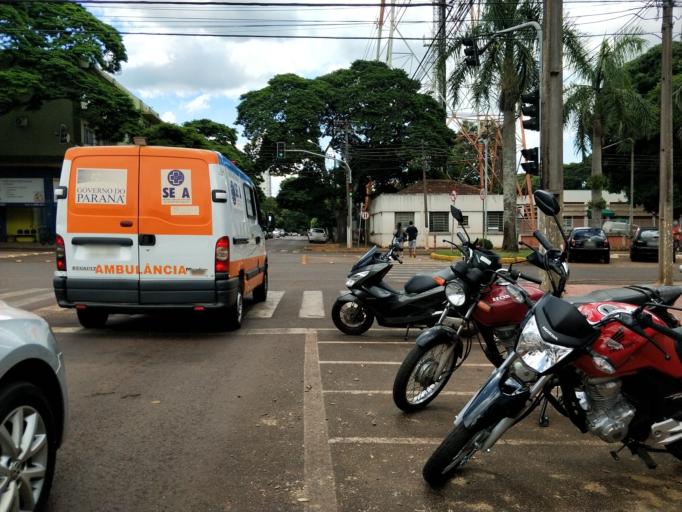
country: BR
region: Parana
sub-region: Marechal Candido Rondon
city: Marechal Candido Rondon
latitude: -24.5589
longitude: -54.0571
